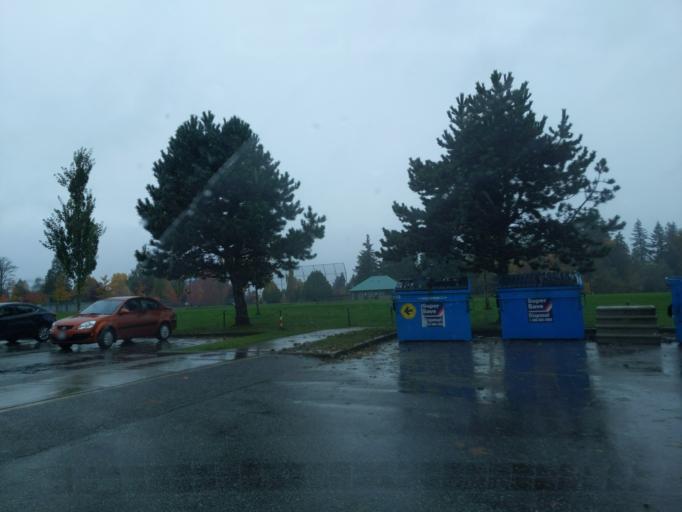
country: CA
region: British Columbia
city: New Westminster
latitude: 49.1935
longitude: -122.8592
